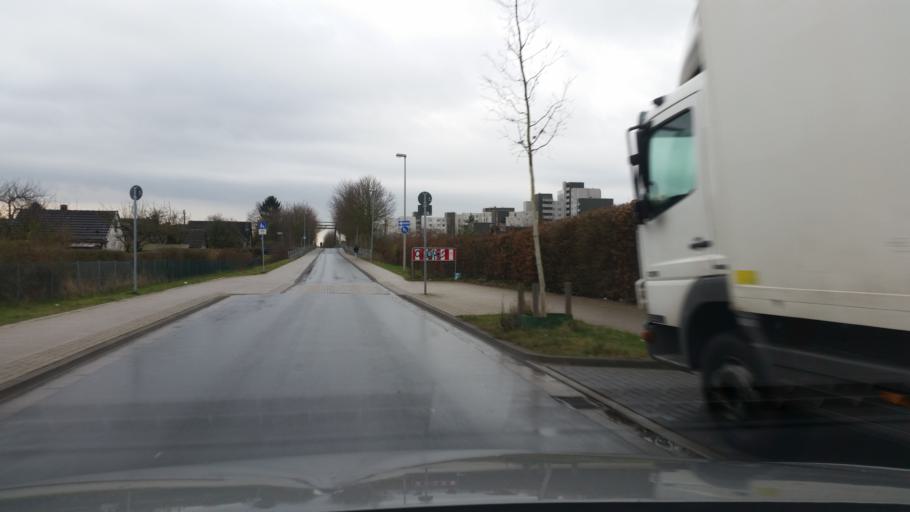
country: DE
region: Lower Saxony
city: Langenhagen
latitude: 52.4087
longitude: 9.7814
